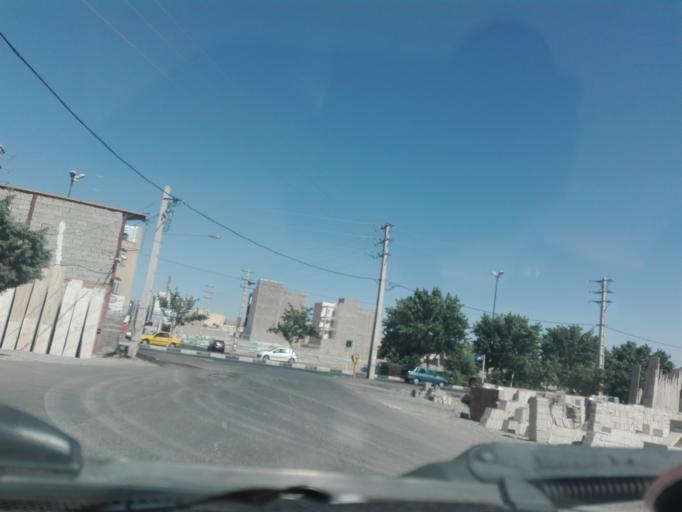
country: IR
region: Tehran
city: Malard
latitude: 35.7194
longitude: 50.9789
